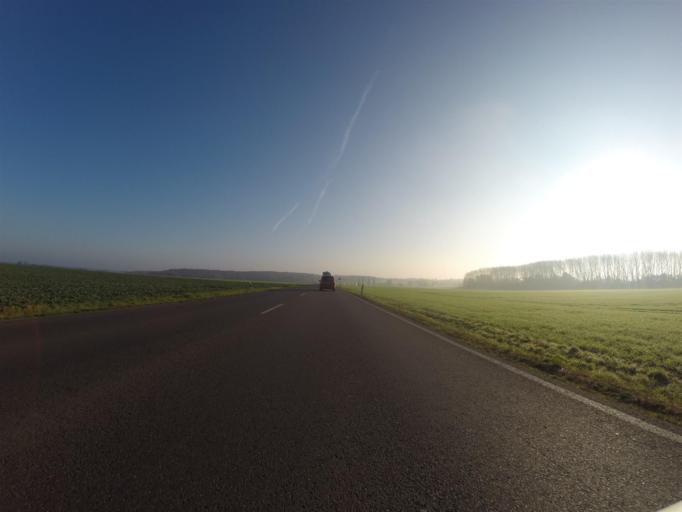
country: DE
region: Saxony
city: Schkeuditz
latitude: 51.3499
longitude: 12.2305
